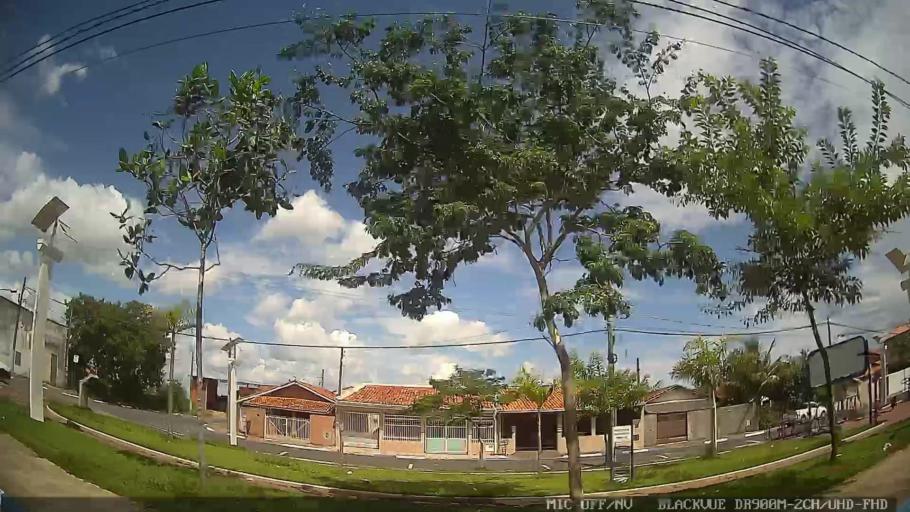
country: BR
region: Sao Paulo
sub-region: Conchas
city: Conchas
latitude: -23.0385
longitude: -48.0188
